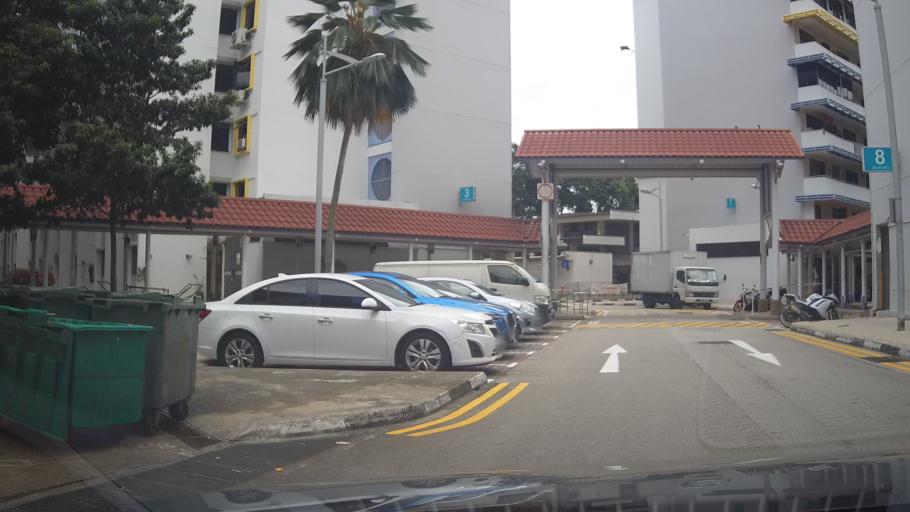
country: SG
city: Singapore
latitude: 1.3030
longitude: 103.8834
